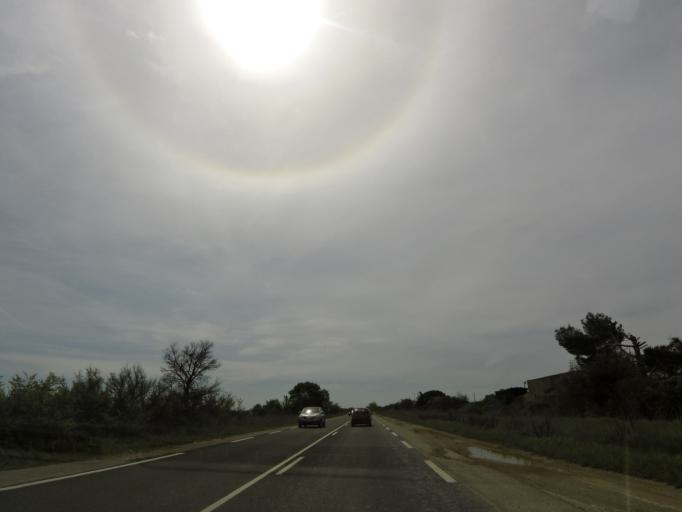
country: FR
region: Languedoc-Roussillon
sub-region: Departement de l'Herault
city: La Grande-Motte
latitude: 43.5958
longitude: 4.1051
